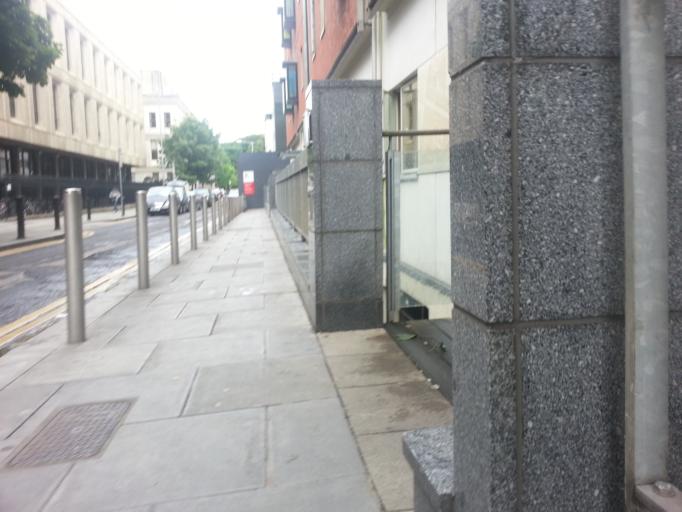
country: IE
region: Leinster
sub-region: Dublin City
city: Dublin
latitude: 53.3391
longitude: -6.2641
